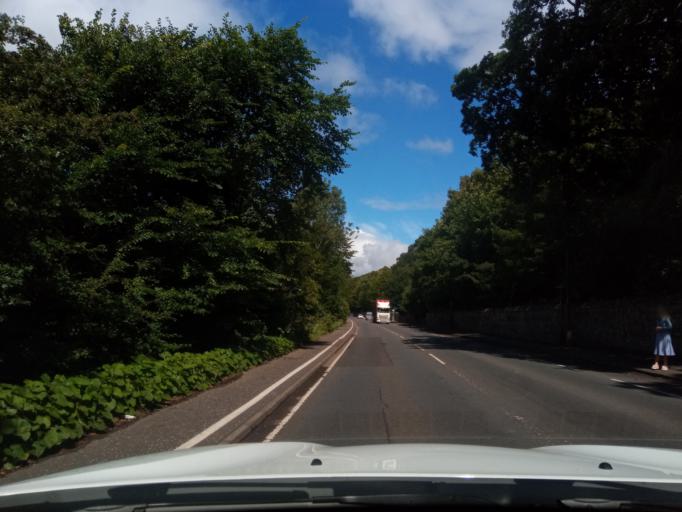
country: GB
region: Scotland
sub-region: Stirling
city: Bridge of Allan
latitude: 56.1415
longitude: -3.9265
